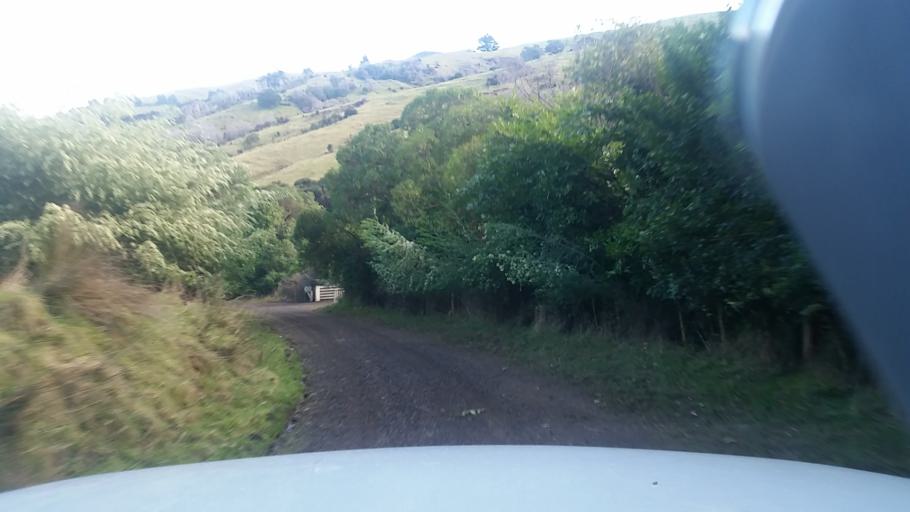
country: NZ
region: Canterbury
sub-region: Christchurch City
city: Christchurch
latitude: -43.7608
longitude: 172.9847
